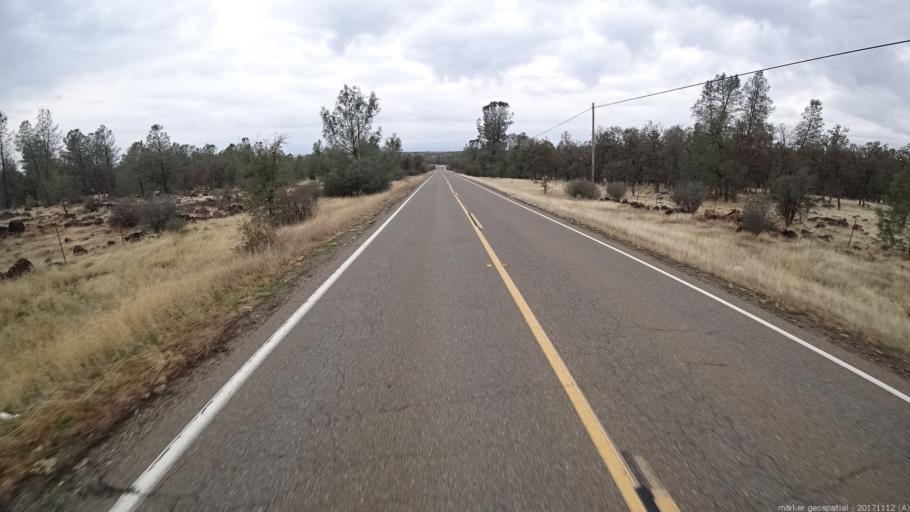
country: US
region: California
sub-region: Shasta County
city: Palo Cedro
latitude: 40.4845
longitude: -122.1135
